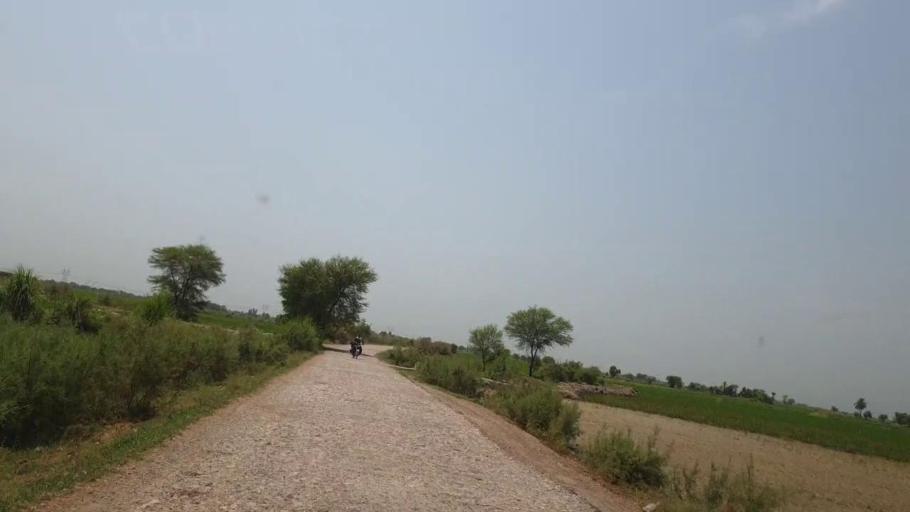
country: PK
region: Sindh
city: Shikarpur
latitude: 27.9031
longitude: 68.6329
